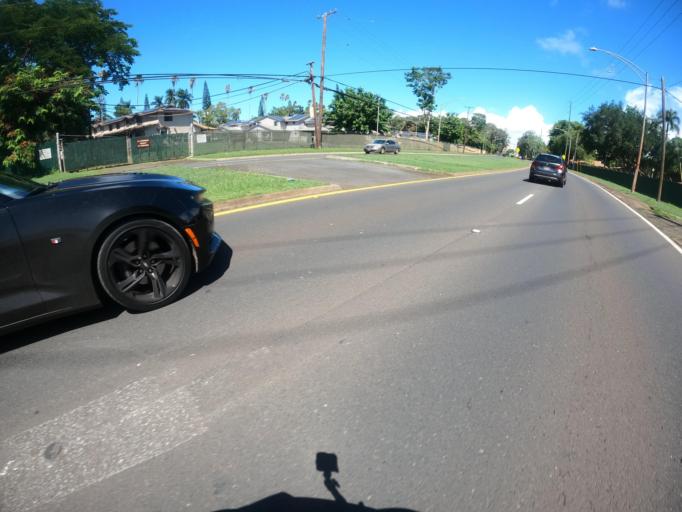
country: US
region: Hawaii
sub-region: Honolulu County
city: Wahiawa
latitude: 21.4855
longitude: -158.0428
